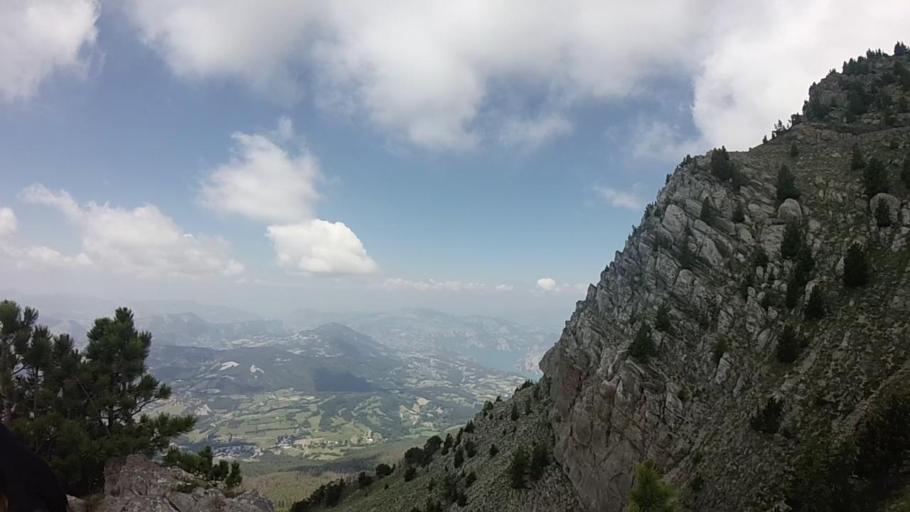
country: FR
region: Provence-Alpes-Cote d'Azur
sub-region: Departement des Alpes-de-Haute-Provence
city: Seyne-les-Alpes
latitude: 44.4068
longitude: 6.3818
